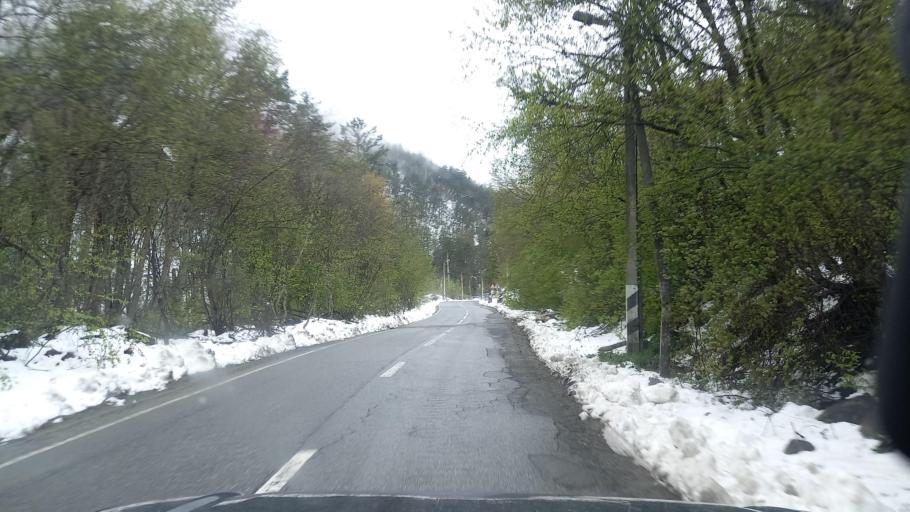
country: RU
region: North Ossetia
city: Mizur
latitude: 42.7943
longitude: 43.9244
